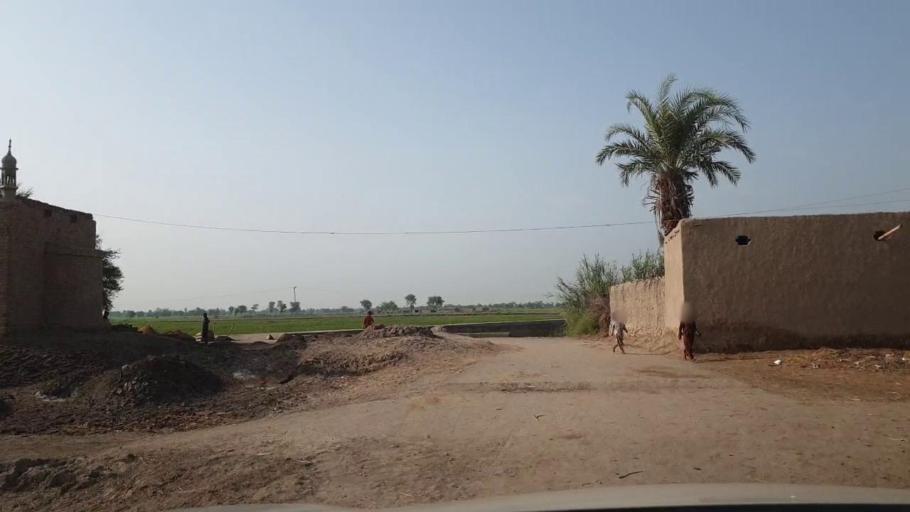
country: PK
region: Sindh
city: Larkana
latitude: 27.4922
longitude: 68.2118
